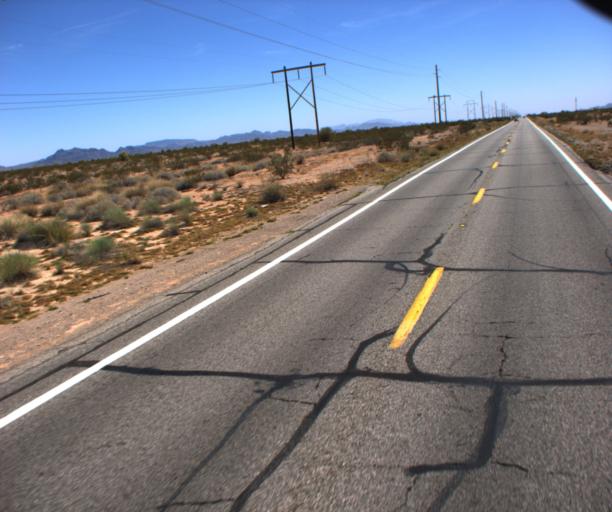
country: US
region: Arizona
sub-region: La Paz County
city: Quartzsite
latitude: 33.8561
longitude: -114.2170
